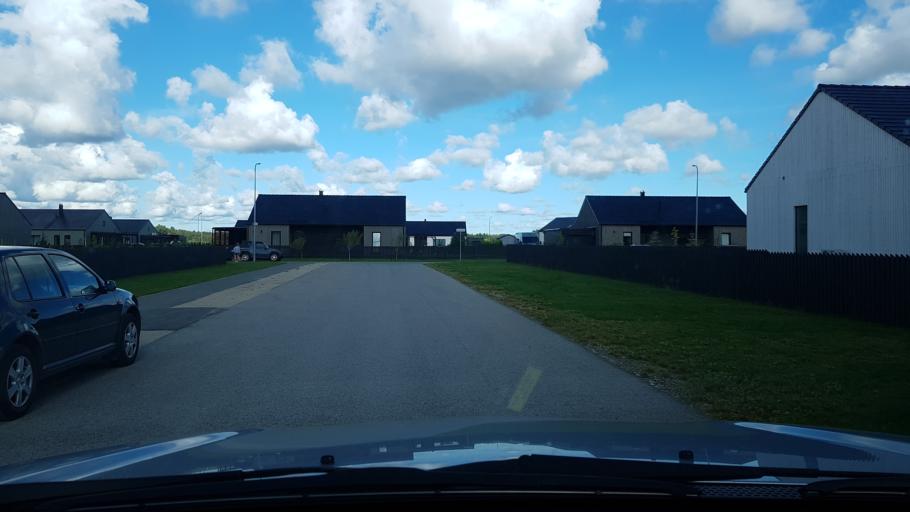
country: EE
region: Harju
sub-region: Kiili vald
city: Kiili
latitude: 59.3613
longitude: 24.8076
